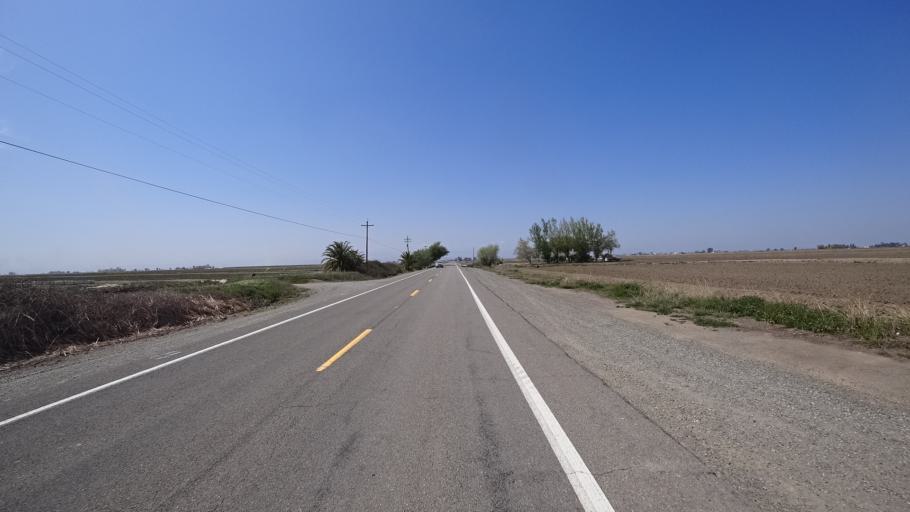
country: US
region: California
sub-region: Glenn County
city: Willows
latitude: 39.5217
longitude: -122.0799
